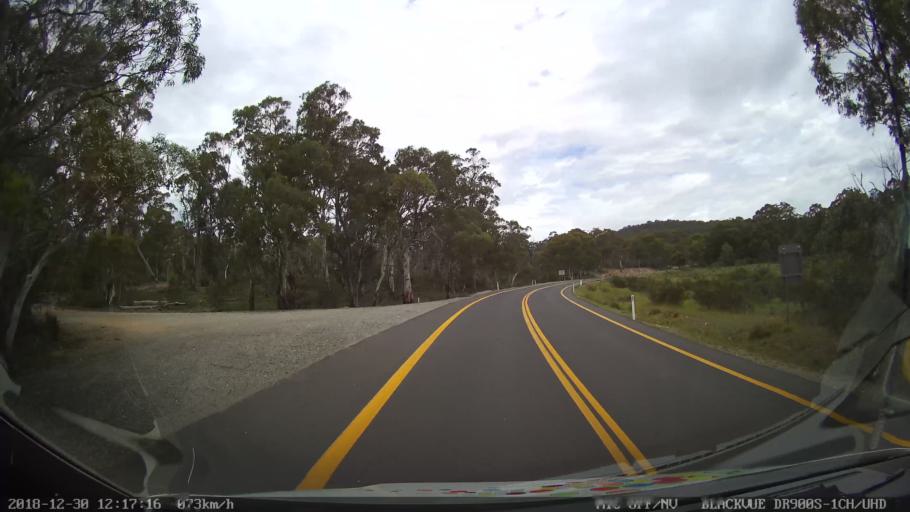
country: AU
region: New South Wales
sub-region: Snowy River
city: Jindabyne
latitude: -36.3533
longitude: 148.5626
